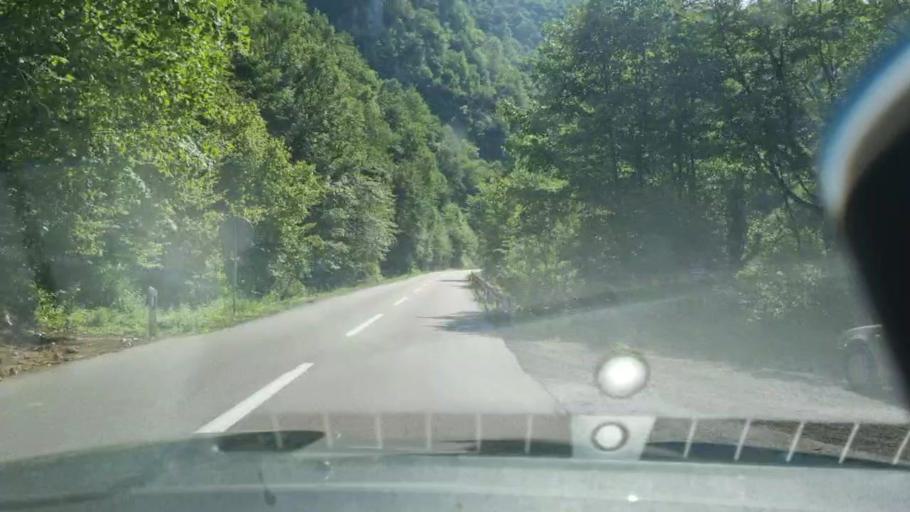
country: BA
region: Federation of Bosnia and Herzegovina
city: Bosanska Krupa
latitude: 44.8661
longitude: 16.0953
